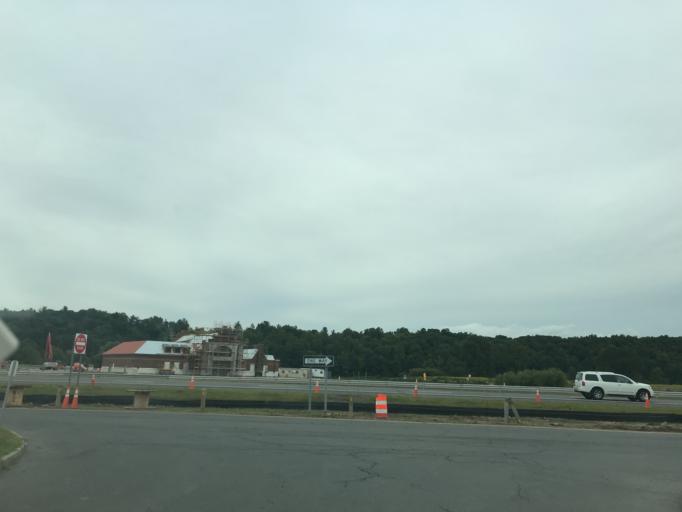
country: US
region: New York
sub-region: Albany County
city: Ravena
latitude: 42.4286
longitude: -73.8051
